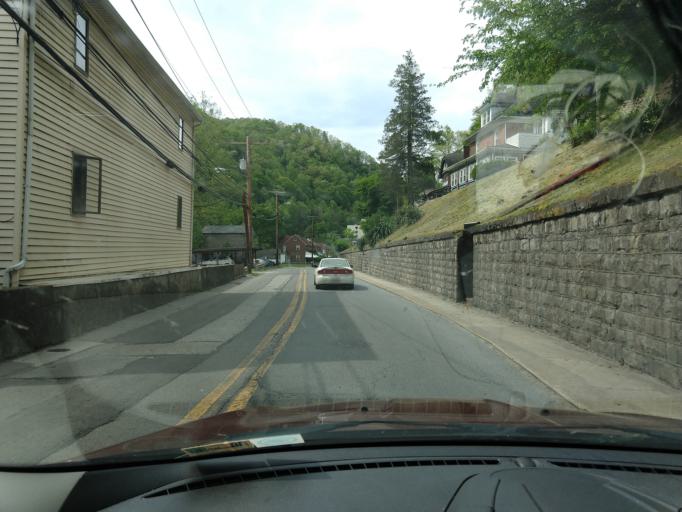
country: US
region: West Virginia
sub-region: McDowell County
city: Welch
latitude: 37.4277
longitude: -81.5845
